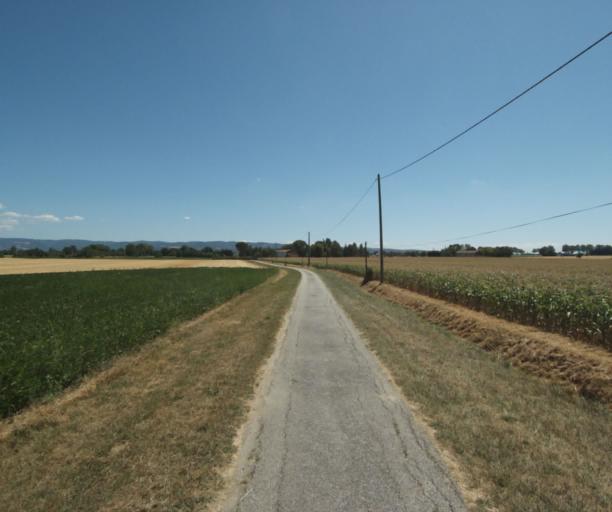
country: FR
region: Midi-Pyrenees
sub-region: Departement de la Haute-Garonne
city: Saint-Felix-Lauragais
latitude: 43.4829
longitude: 1.9357
